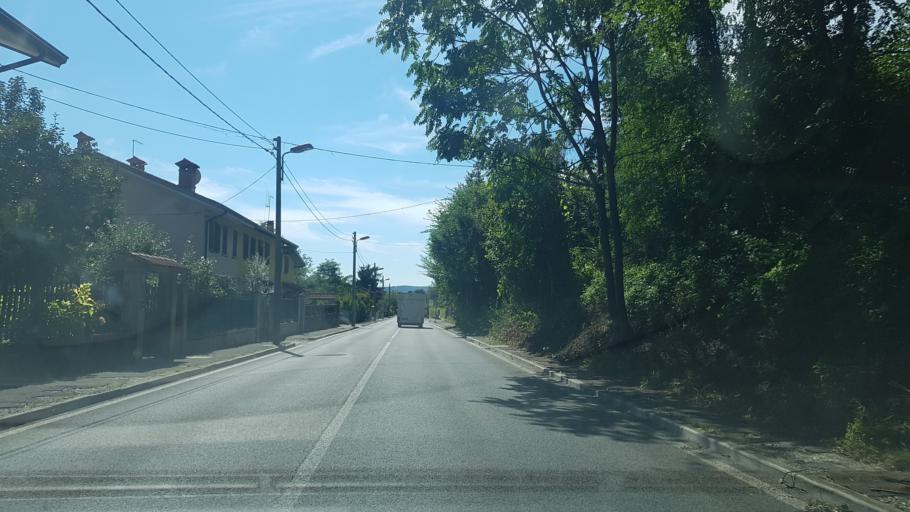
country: IT
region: Friuli Venezia Giulia
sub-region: Provincia di Gorizia
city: Gorizia
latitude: 45.9531
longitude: 13.6062
